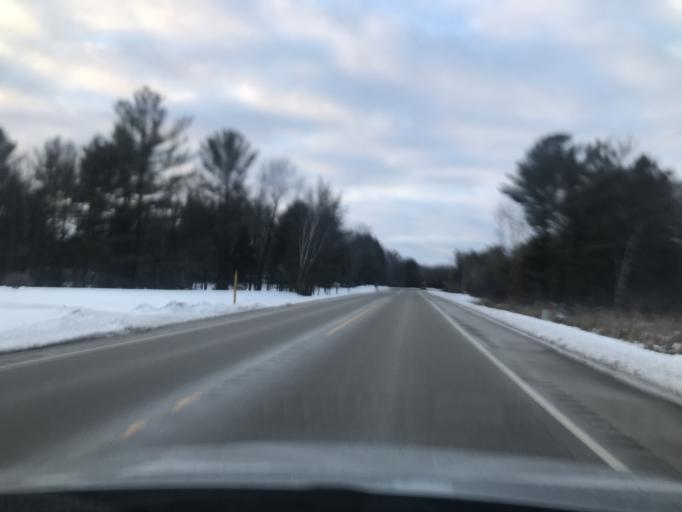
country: US
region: Wisconsin
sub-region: Marinette County
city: Marinette
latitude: 45.1144
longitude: -87.6771
